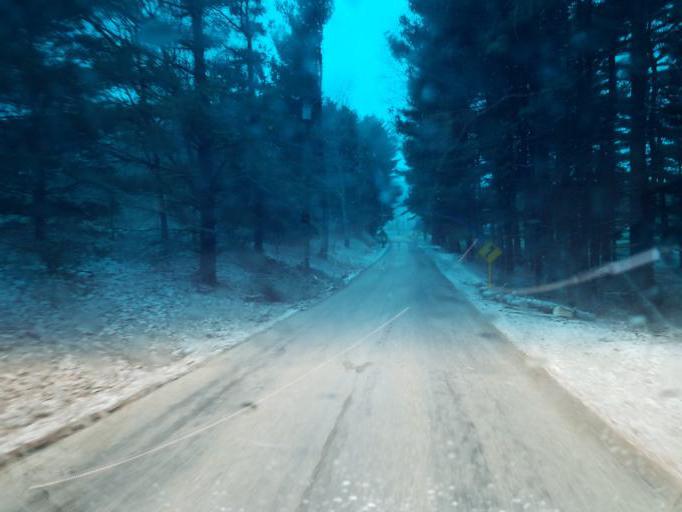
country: US
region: Ohio
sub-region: Sandusky County
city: Bellville
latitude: 40.6269
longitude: -82.5537
